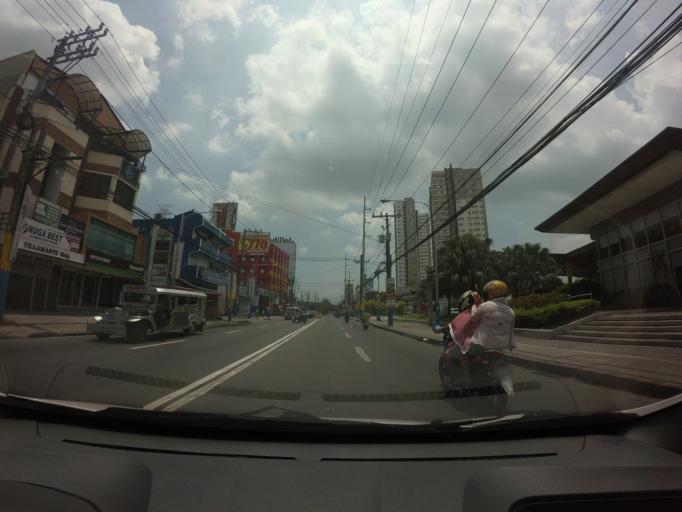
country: PH
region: Calabarzon
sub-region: Province of Laguna
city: San Pedro
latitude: 14.4125
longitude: 121.0460
